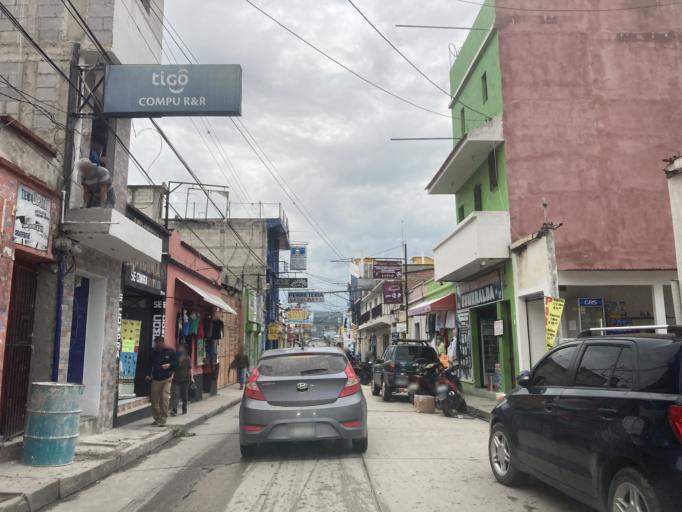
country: GT
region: Huehuetenango
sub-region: Municipio de Huehuetenango
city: Huehuetenango
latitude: 15.3228
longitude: -91.4688
